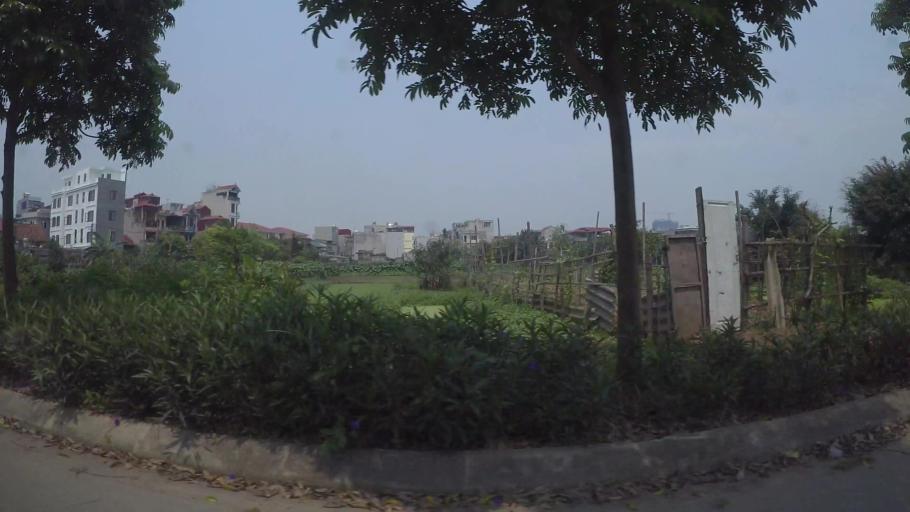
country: VN
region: Ha Noi
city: Van Dien
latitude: 20.9505
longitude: 105.8371
